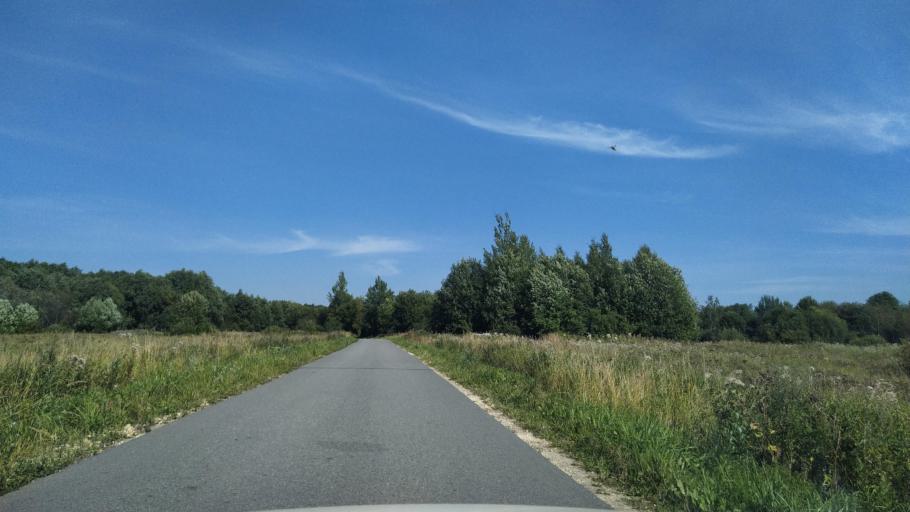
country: RU
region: Leningrad
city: Rozhdestveno
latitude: 59.2622
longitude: 30.0270
